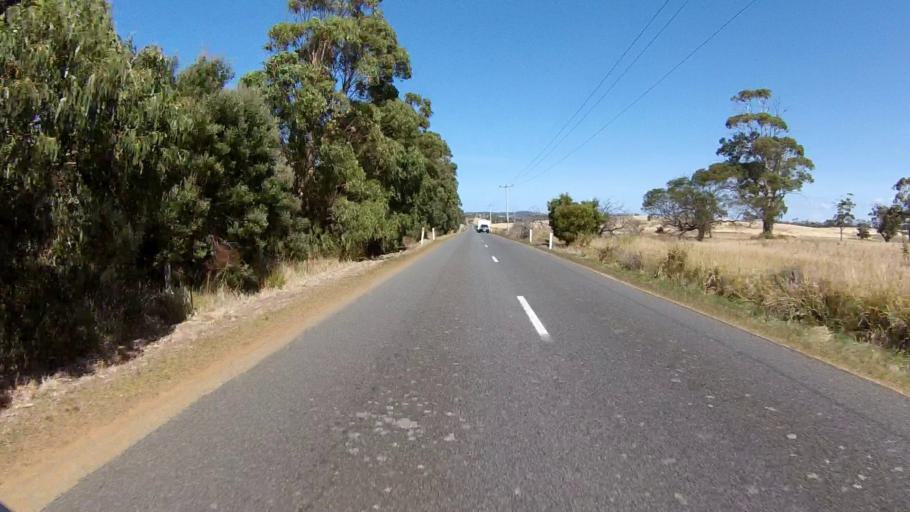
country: AU
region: Tasmania
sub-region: Sorell
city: Sorell
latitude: -42.2719
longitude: 148.0040
